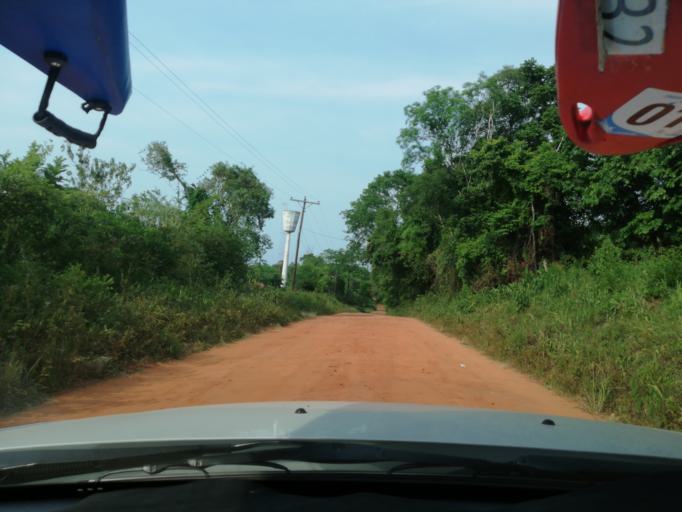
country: AR
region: Misiones
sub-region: Departamento de San Ignacio
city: San Ignacio
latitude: -27.2968
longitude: -55.5715
